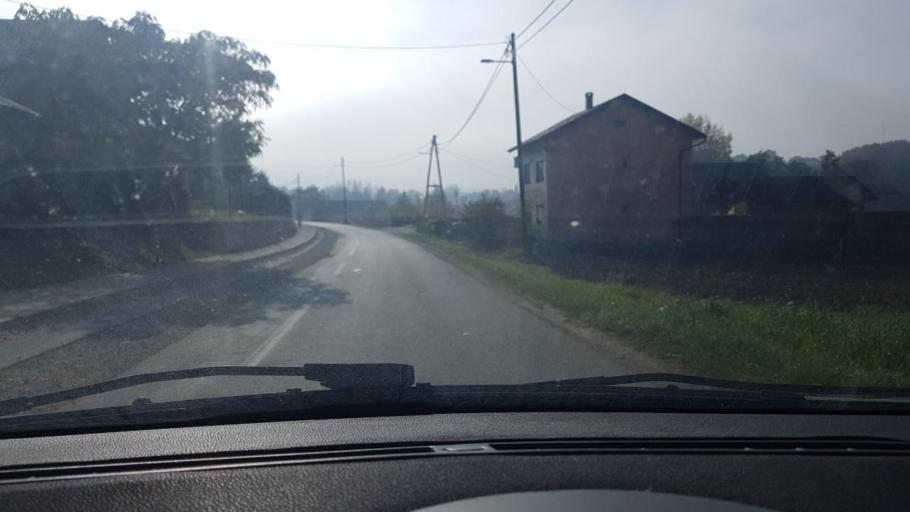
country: HR
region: Krapinsko-Zagorska
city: Zlatar
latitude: 46.1476
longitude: 16.0669
